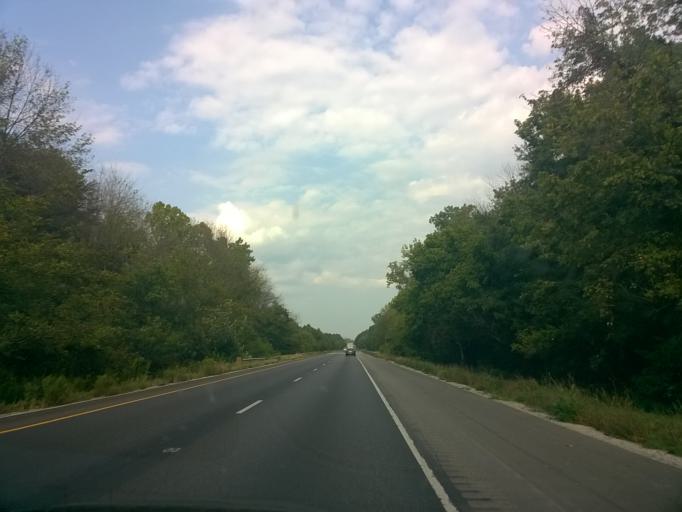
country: US
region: Indiana
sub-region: Clay County
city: Brazil
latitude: 39.4571
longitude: -87.0907
